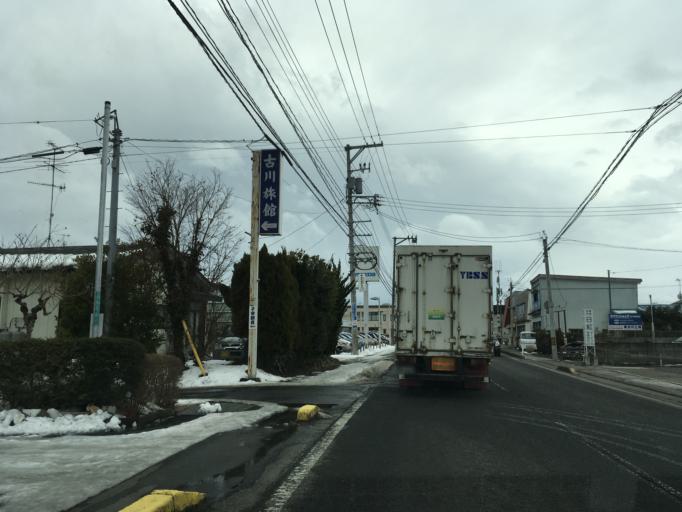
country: JP
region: Miyagi
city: Furukawa
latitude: 38.5831
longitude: 140.9661
